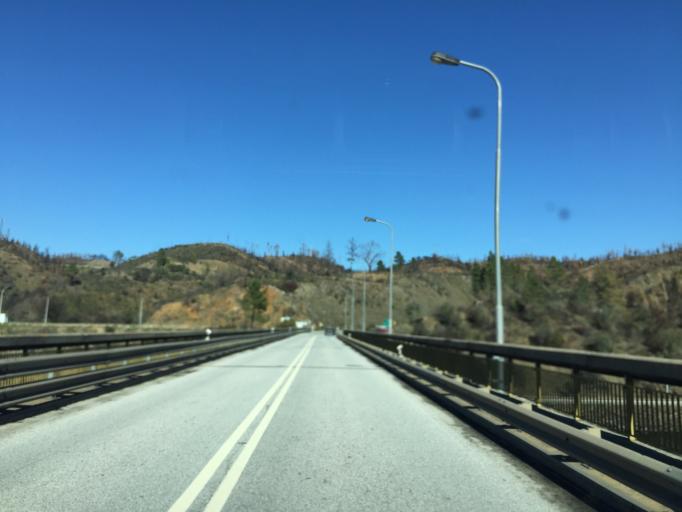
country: PT
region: Portalegre
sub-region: Gaviao
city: Gaviao
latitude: 39.5434
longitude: -7.8027
